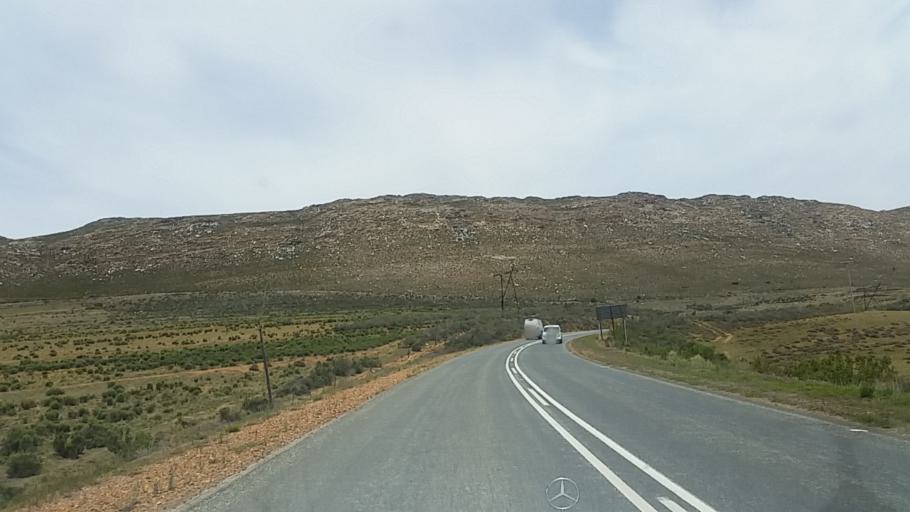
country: ZA
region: Western Cape
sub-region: Eden District Municipality
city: Knysna
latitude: -33.7379
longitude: 23.0394
